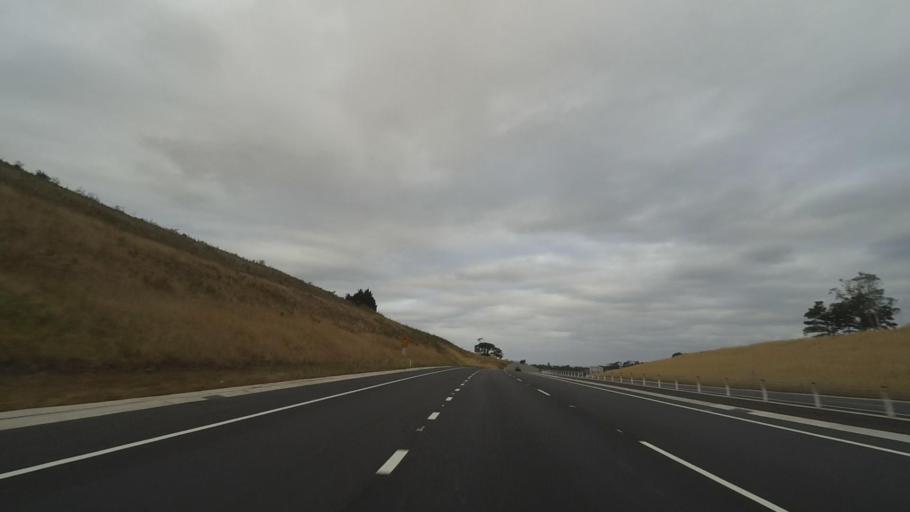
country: AU
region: New South Wales
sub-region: Kiama
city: Gerringong
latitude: -34.7484
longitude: 150.7992
